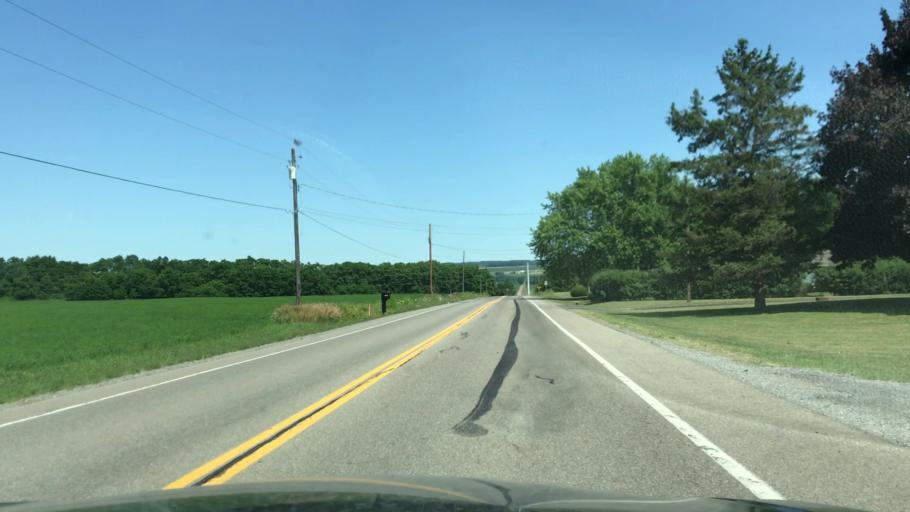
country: US
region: New York
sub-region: Livingston County
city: Mount Morris
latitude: 42.7563
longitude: -77.8901
